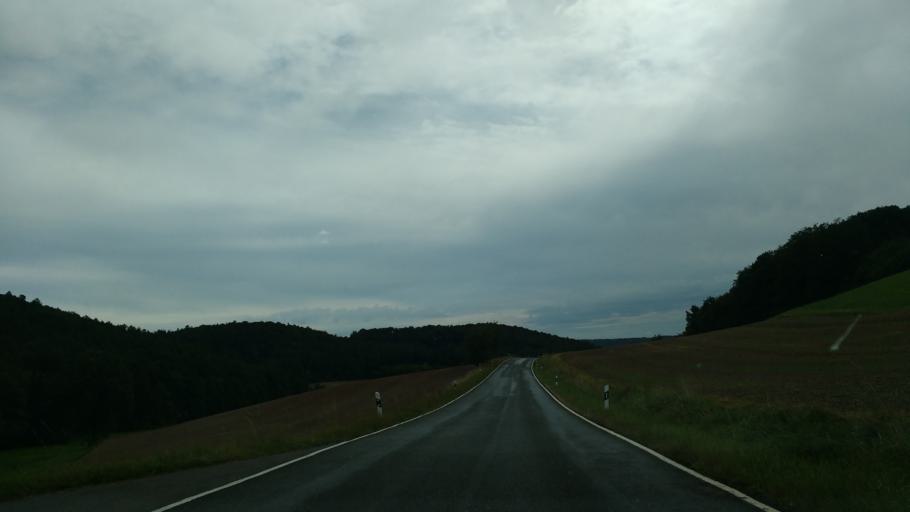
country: DE
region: Bavaria
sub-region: Regierungsbezirk Unterfranken
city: Geiselwind
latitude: 49.7951
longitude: 10.4952
